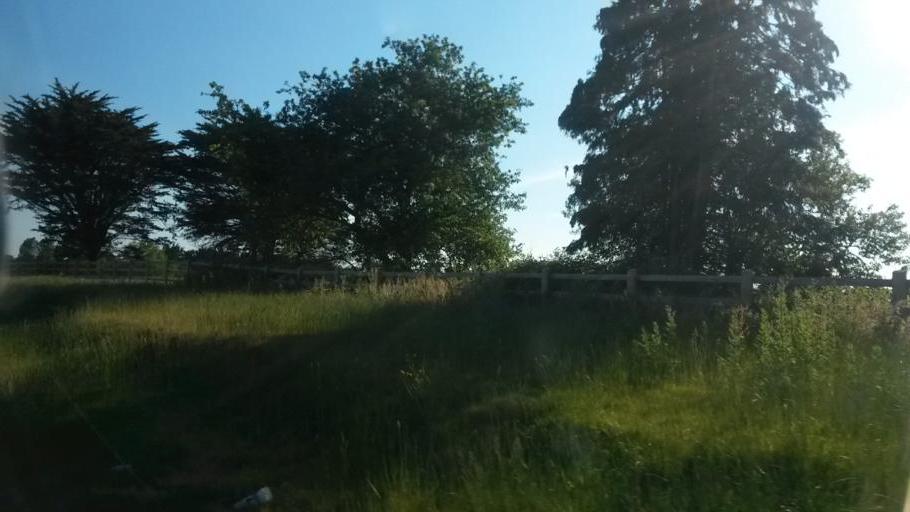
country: IE
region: Leinster
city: Ballymun
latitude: 53.4394
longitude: -6.2934
